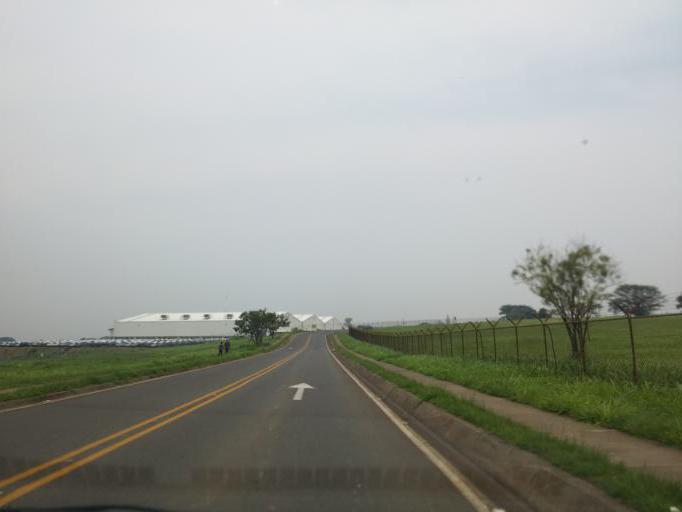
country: CR
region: Heredia
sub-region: Canton de Belen
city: San Antonio
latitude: 9.9960
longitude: -84.1951
